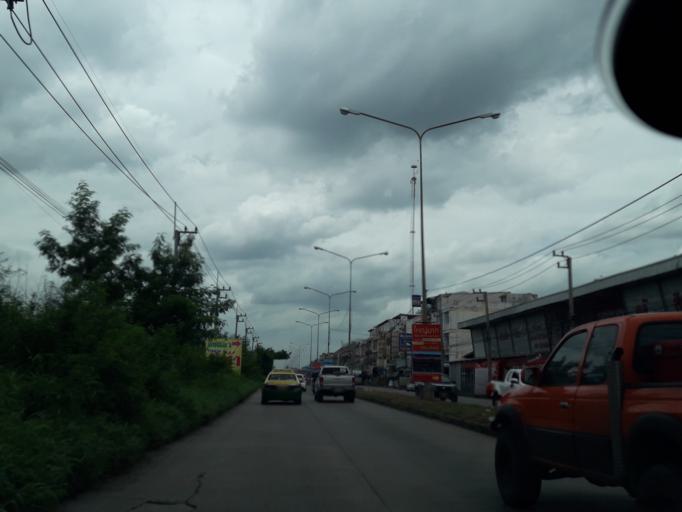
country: TH
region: Pathum Thani
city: Khlong Luang
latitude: 14.0692
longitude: 100.6339
